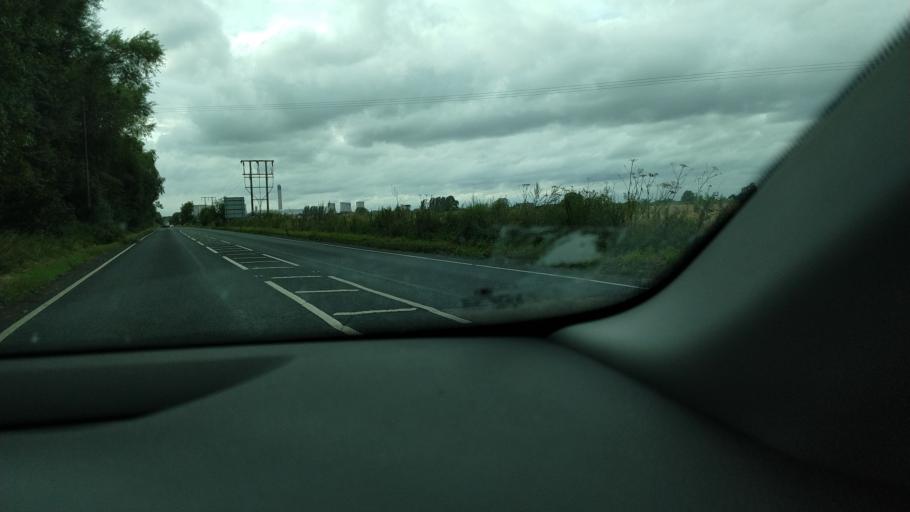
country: GB
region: England
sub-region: East Riding of Yorkshire
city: Rawcliffe
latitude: 53.7068
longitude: -0.9370
